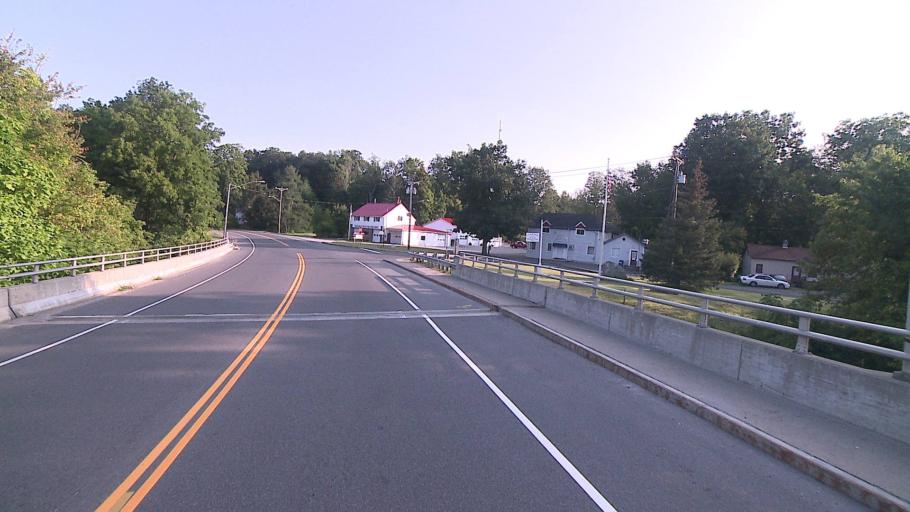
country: US
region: Connecticut
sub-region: Fairfield County
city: Sherman
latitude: 41.6476
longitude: -73.4838
